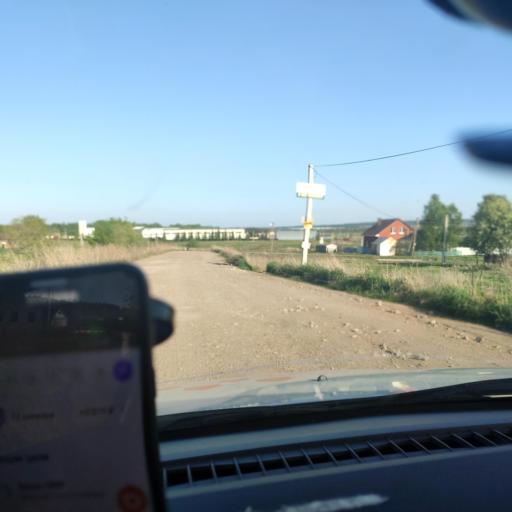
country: RU
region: Bashkortostan
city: Avdon
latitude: 54.5122
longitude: 55.8140
